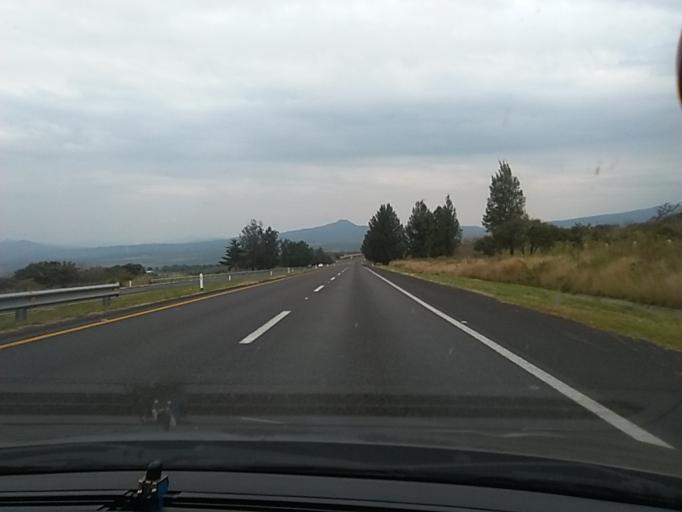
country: MX
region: Michoacan
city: Penjamillo de Degollado
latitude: 20.0775
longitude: -101.9765
